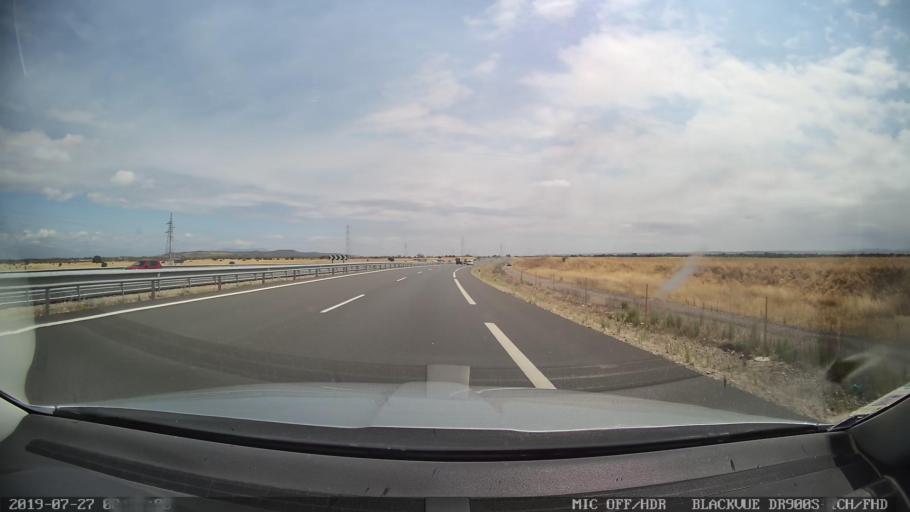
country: ES
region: Castille-La Mancha
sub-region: Province of Toledo
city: Velada
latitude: 39.9322
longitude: -5.0033
